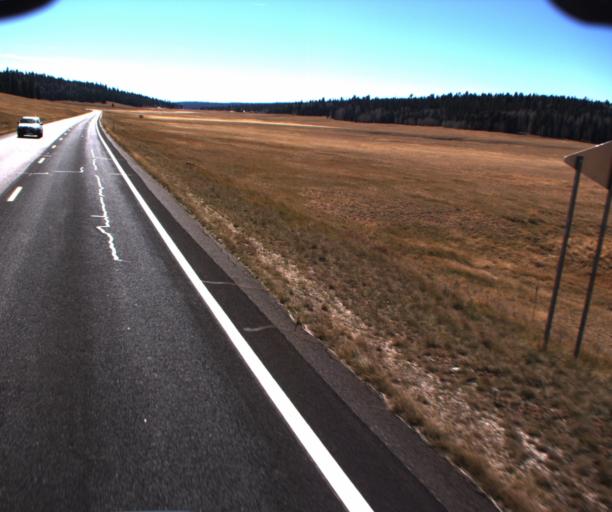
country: US
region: Arizona
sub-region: Coconino County
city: Grand Canyon
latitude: 36.4321
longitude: -112.1329
